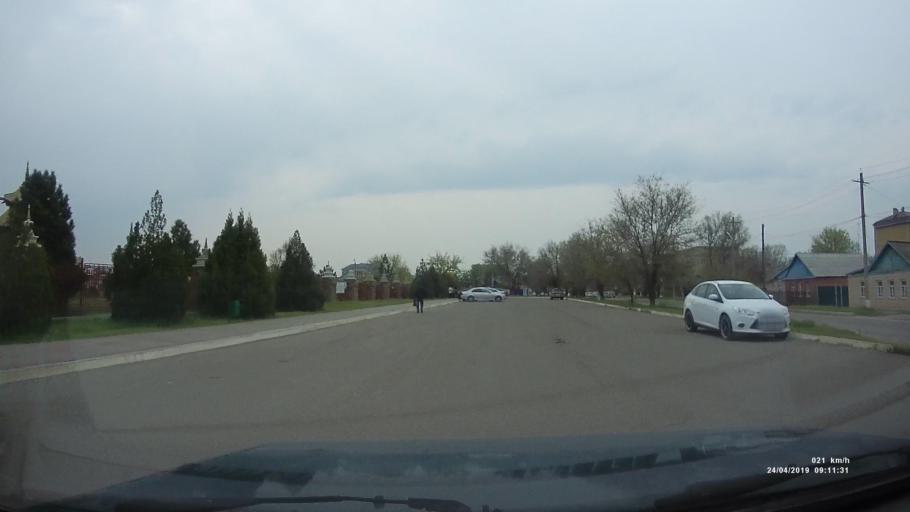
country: RU
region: Kalmykiya
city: Elista
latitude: 46.3092
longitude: 44.2825
